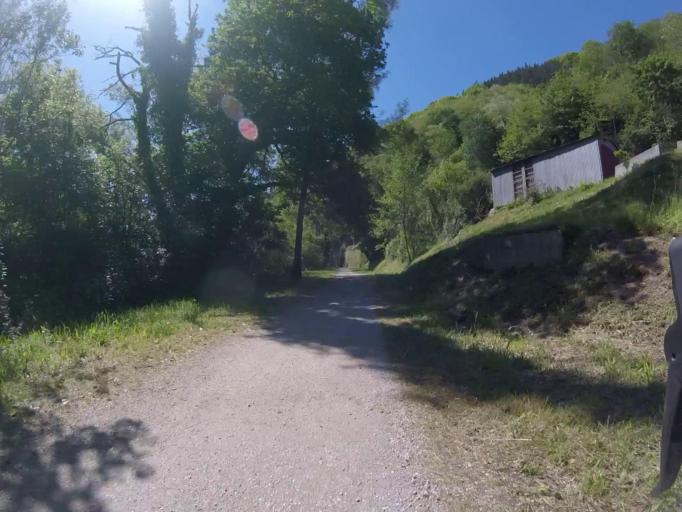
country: ES
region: Basque Country
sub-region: Provincia de Guipuzcoa
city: Irun
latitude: 43.3171
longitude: -1.7421
